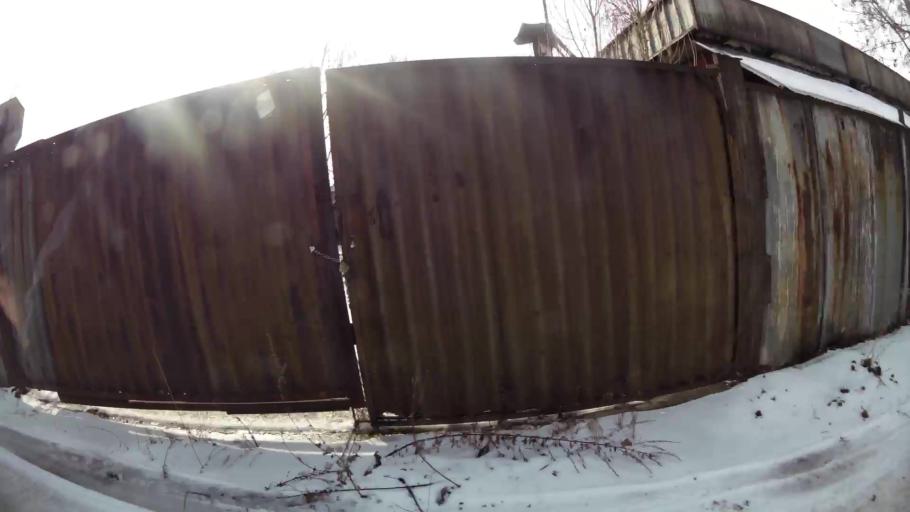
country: BG
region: Sofia-Capital
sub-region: Stolichna Obshtina
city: Sofia
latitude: 42.7050
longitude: 23.3434
